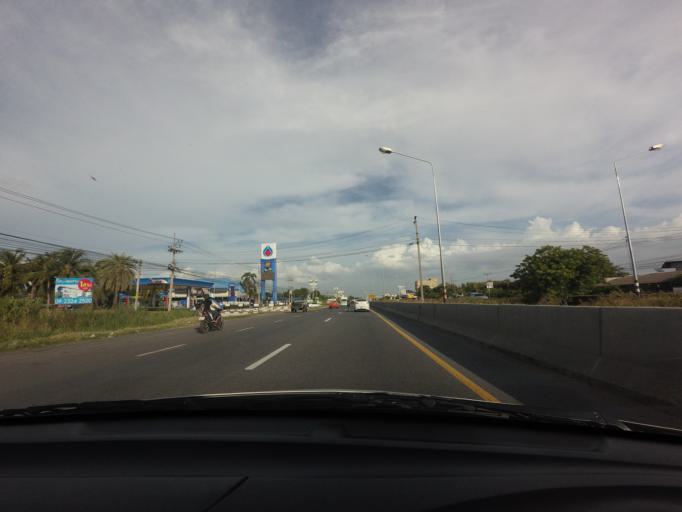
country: TH
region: Nonthaburi
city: Bang Bua Thong
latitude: 13.9736
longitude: 100.3936
